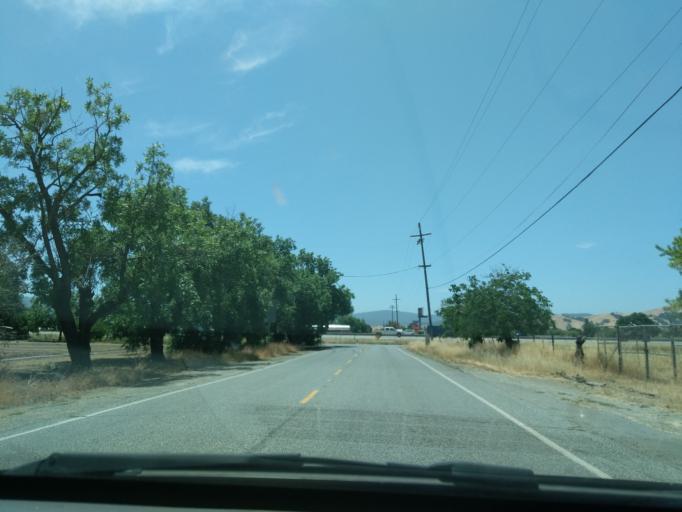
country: US
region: California
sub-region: Santa Clara County
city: San Martin
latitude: 37.0540
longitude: -121.5806
